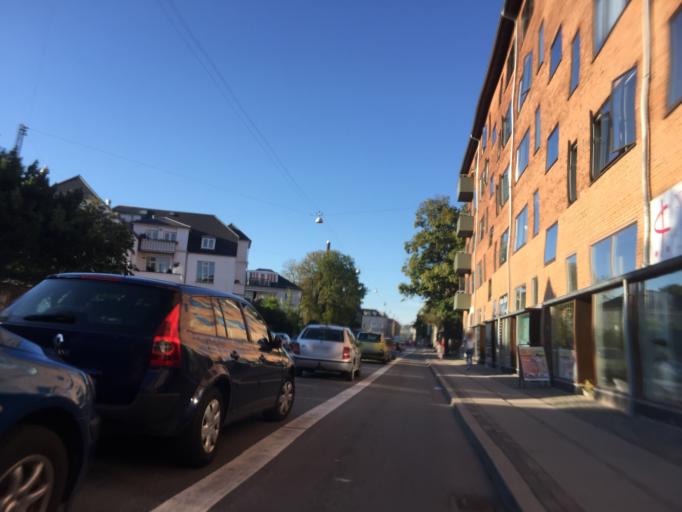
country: DK
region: Capital Region
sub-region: Frederiksberg Kommune
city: Frederiksberg
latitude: 55.6767
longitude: 12.5204
